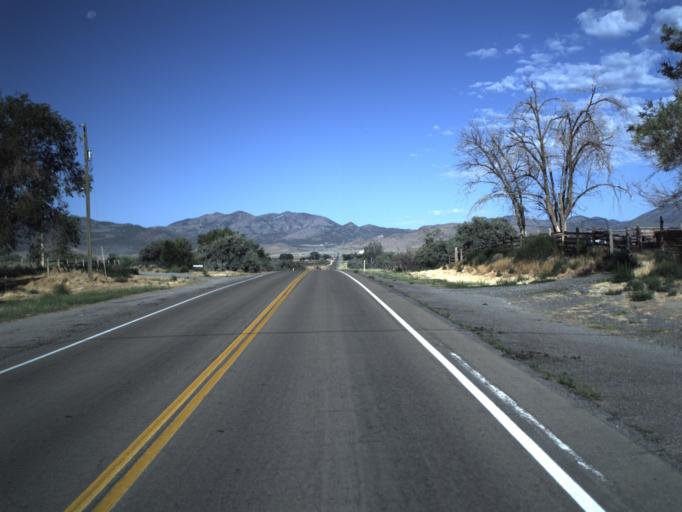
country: US
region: Utah
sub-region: Utah County
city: Genola
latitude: 39.9524
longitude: -111.9268
